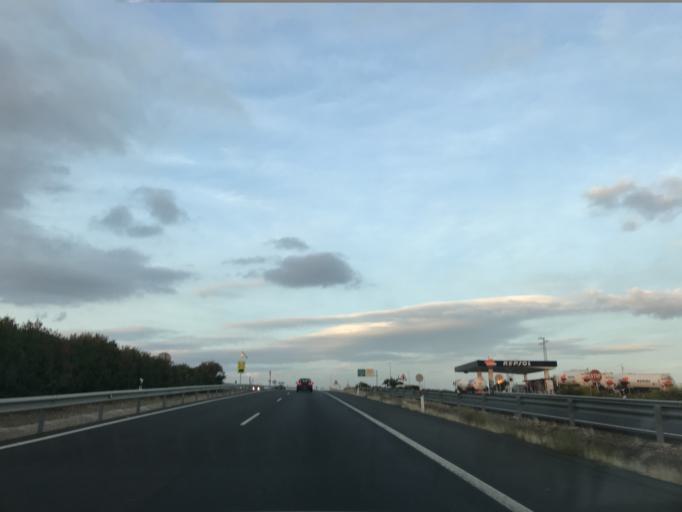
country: ES
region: Andalusia
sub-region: Province of Cordoba
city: La Victoria
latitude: 37.7576
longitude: -4.8292
